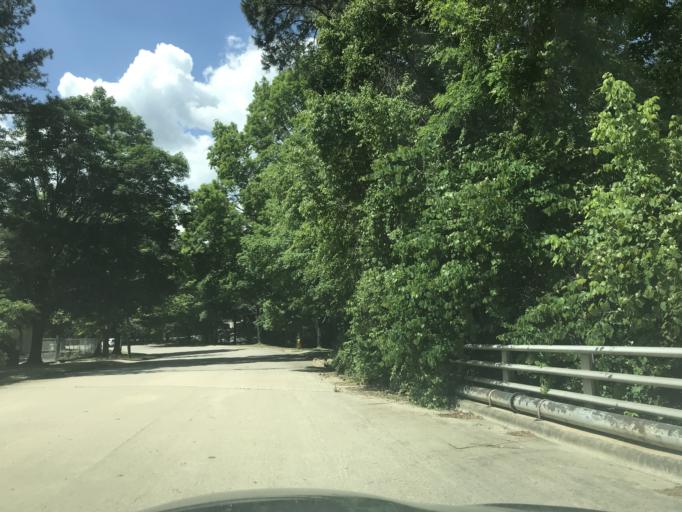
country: US
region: North Carolina
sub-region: Wake County
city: West Raleigh
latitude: 35.8381
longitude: -78.6720
